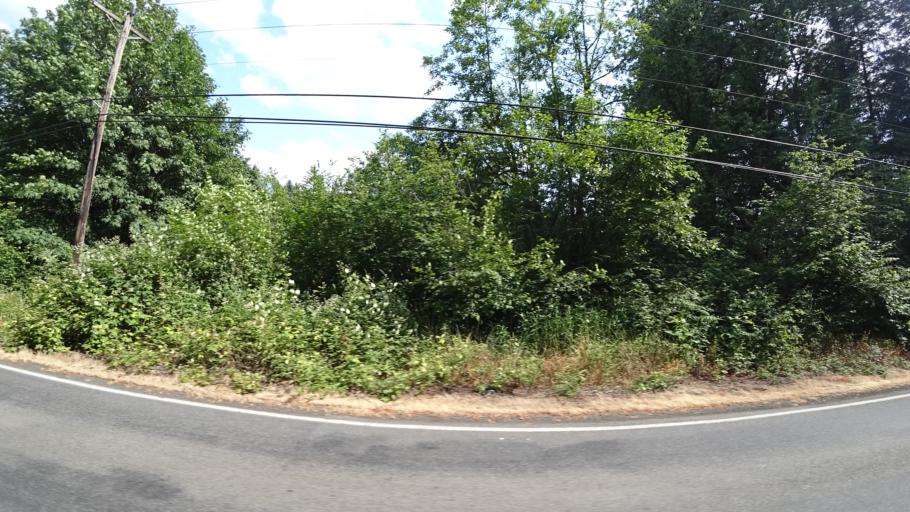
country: US
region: Oregon
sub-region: Washington County
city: Oak Hills
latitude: 45.5840
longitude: -122.8090
